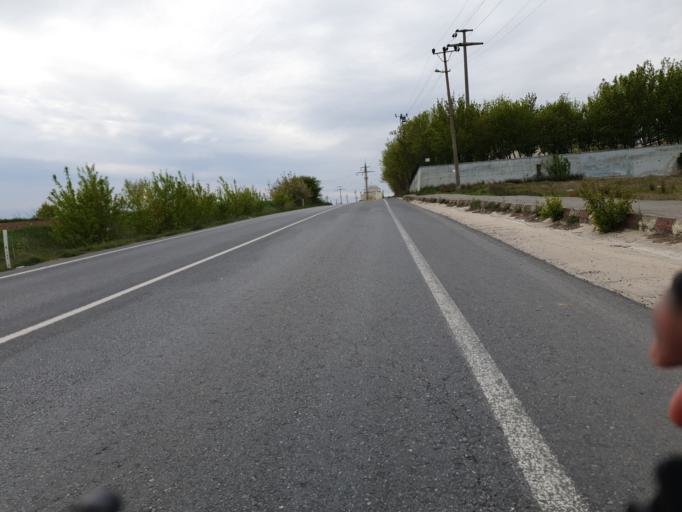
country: TR
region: Tekirdag
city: Saray
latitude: 41.4496
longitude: 27.9264
